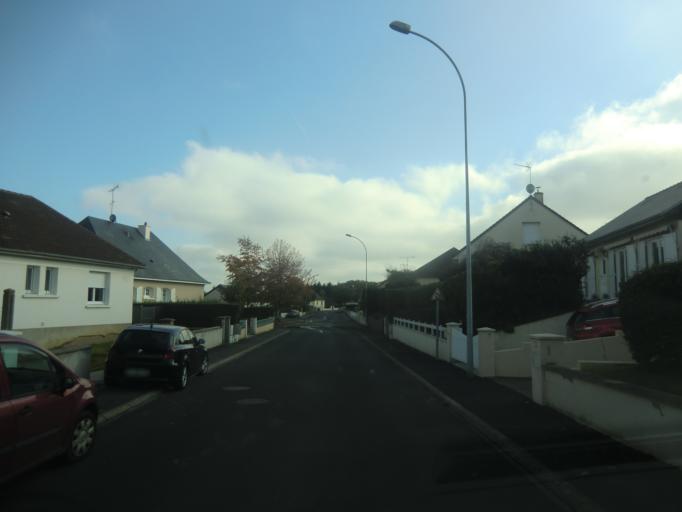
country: FR
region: Pays de la Loire
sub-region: Departement de la Mayenne
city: Chateau-Gontier
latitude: 47.8191
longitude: -0.7021
